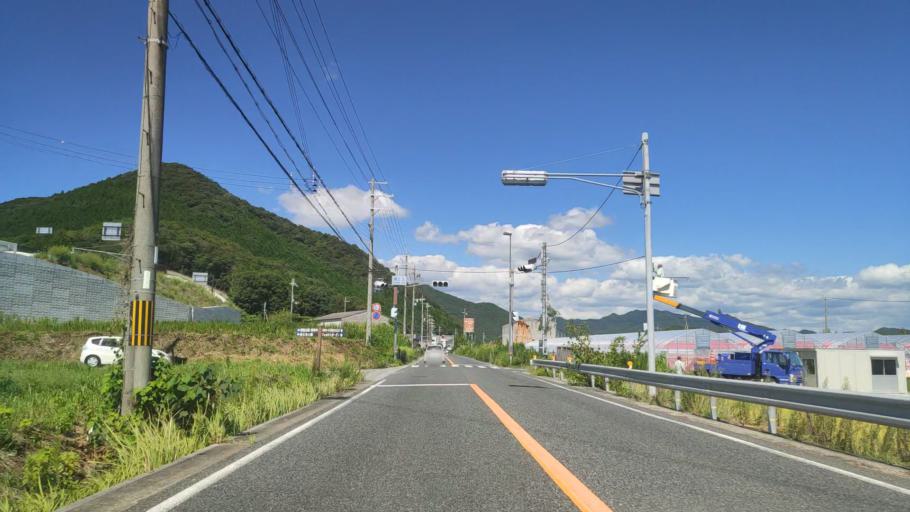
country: JP
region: Hyogo
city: Nishiwaki
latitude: 35.0119
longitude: 134.9907
